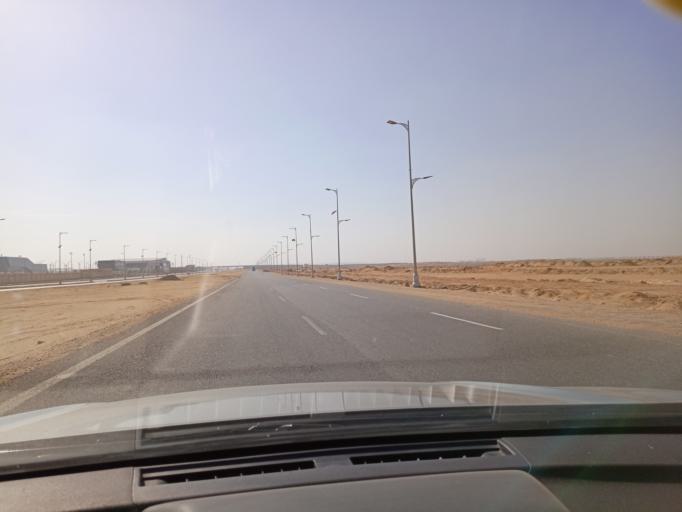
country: EG
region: Muhafazat al Qalyubiyah
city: Al Khankah
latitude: 30.0444
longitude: 31.7004
